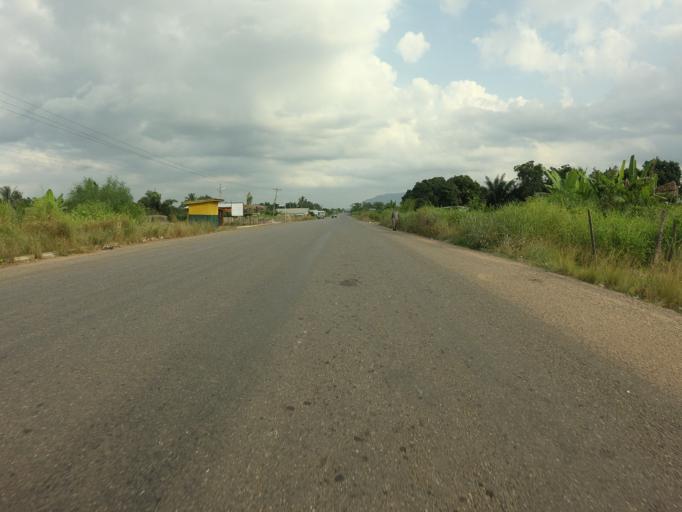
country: GH
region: Volta
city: Ho
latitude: 6.5786
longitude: 0.4825
